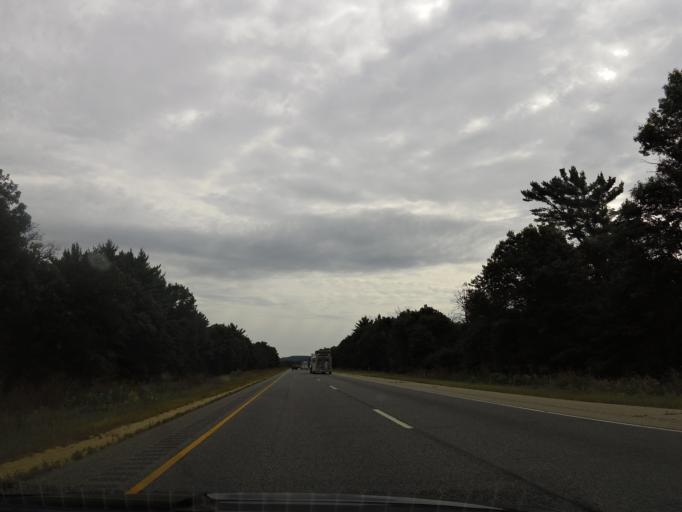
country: US
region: Wisconsin
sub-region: Monroe County
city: Sparta
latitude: 43.9430
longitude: -90.6946
